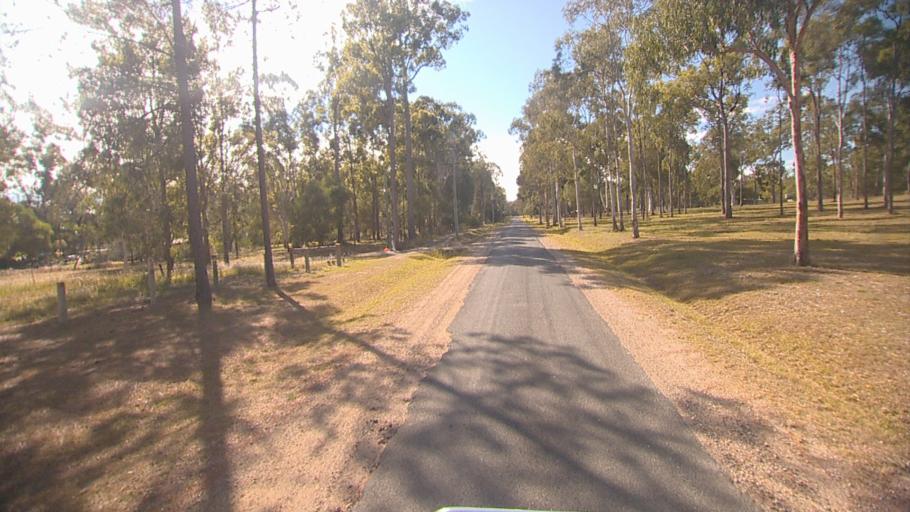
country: AU
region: Queensland
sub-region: Logan
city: Chambers Flat
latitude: -27.7864
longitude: 153.0693
